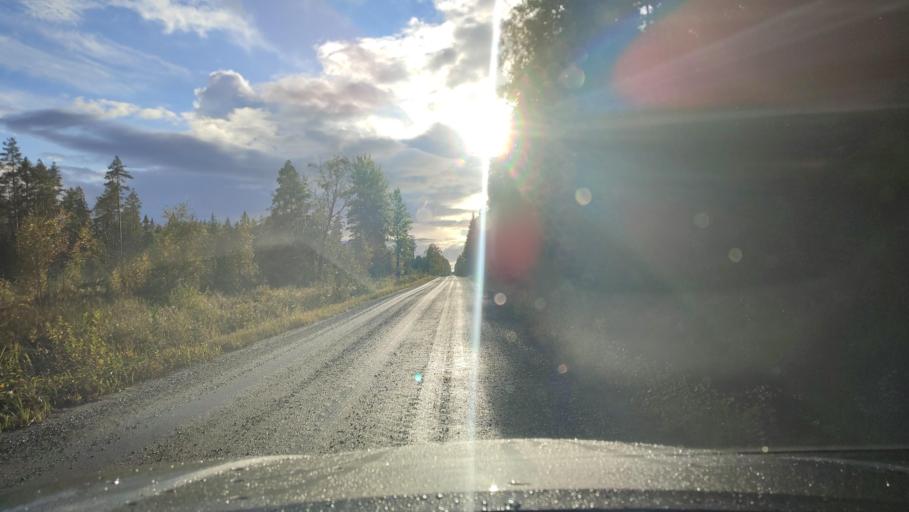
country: FI
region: Ostrobothnia
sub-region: Sydosterbotten
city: Kristinestad
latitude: 62.3061
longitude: 21.5327
